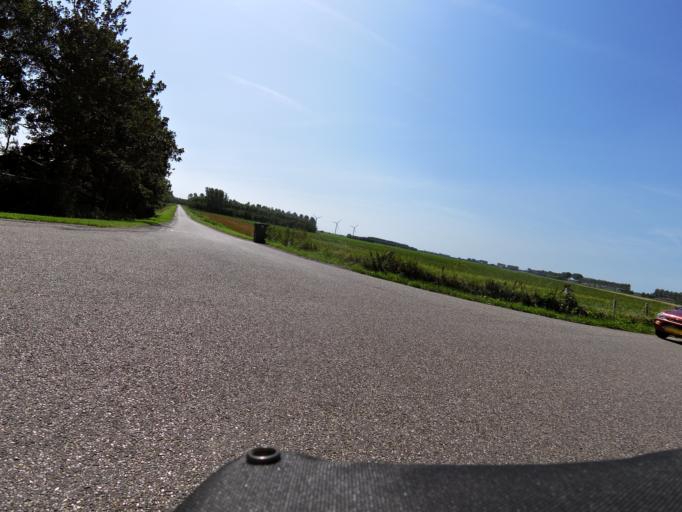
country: NL
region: South Holland
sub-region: Gemeente Goeree-Overflakkee
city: Middelharnis
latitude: 51.7178
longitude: 4.1429
